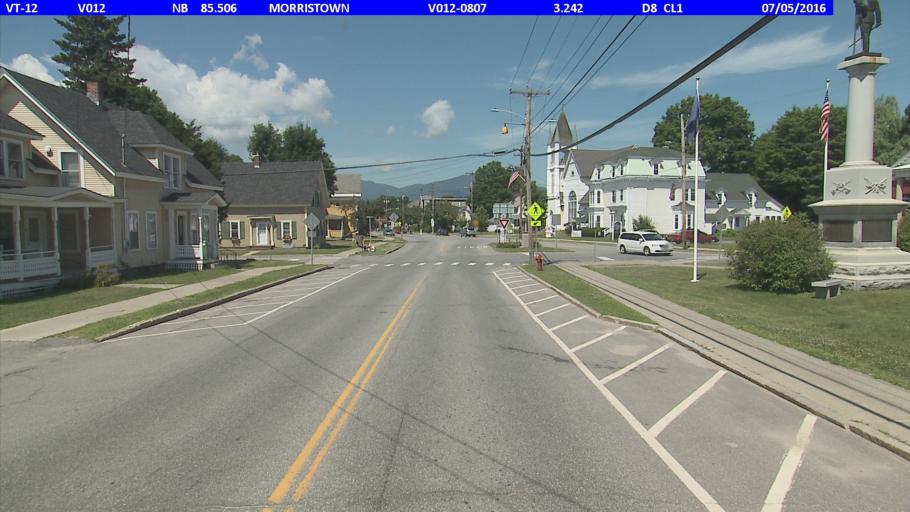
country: US
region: Vermont
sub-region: Lamoille County
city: Morrisville
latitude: 44.5617
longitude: -72.5952
